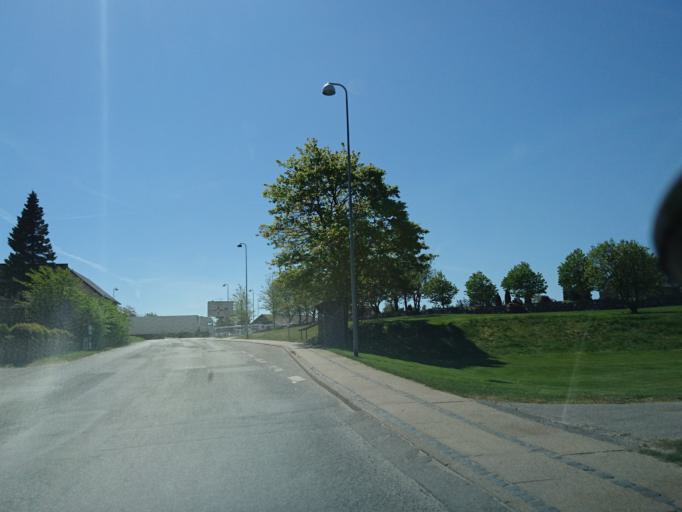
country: DK
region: North Denmark
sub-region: Hjorring Kommune
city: Sindal
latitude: 57.5821
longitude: 10.1841
